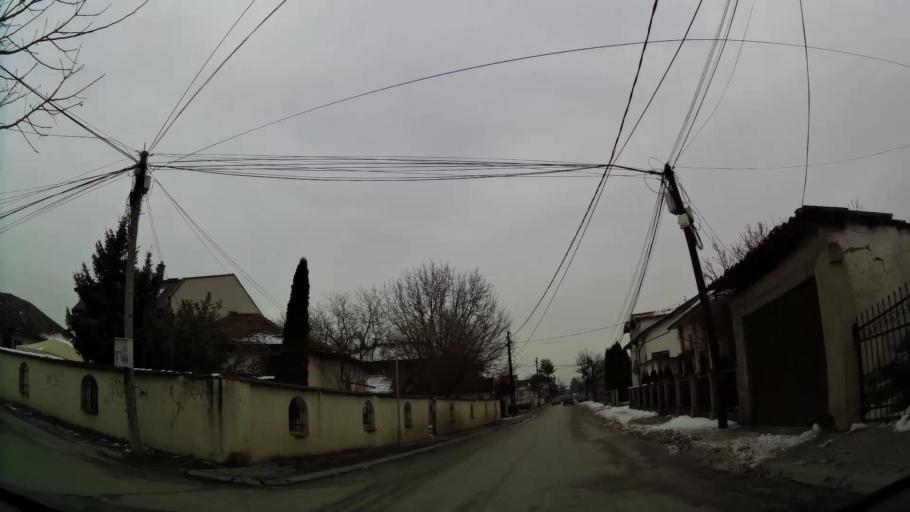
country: MK
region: Butel
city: Butel
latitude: 42.0367
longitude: 21.4480
